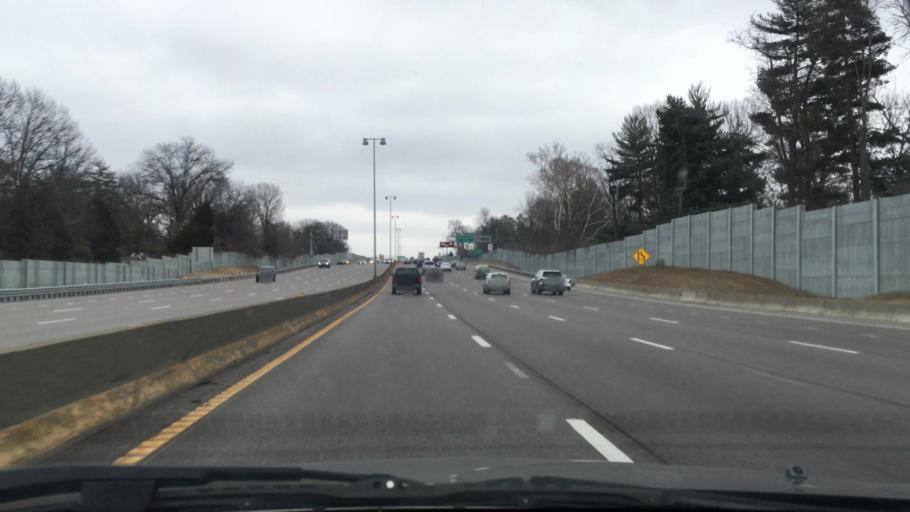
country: US
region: Missouri
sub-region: Saint Louis County
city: Frontenac
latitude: 38.6378
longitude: -90.4345
